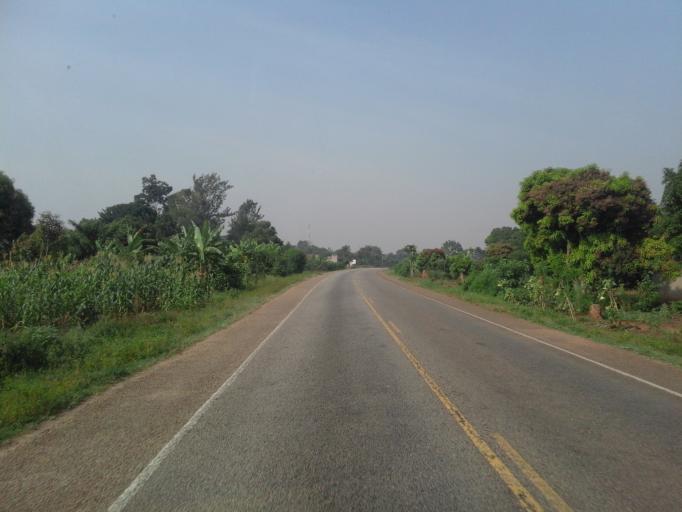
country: UG
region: Eastern Region
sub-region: Budaka District
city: Budaka
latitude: 1.0234
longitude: 33.9742
